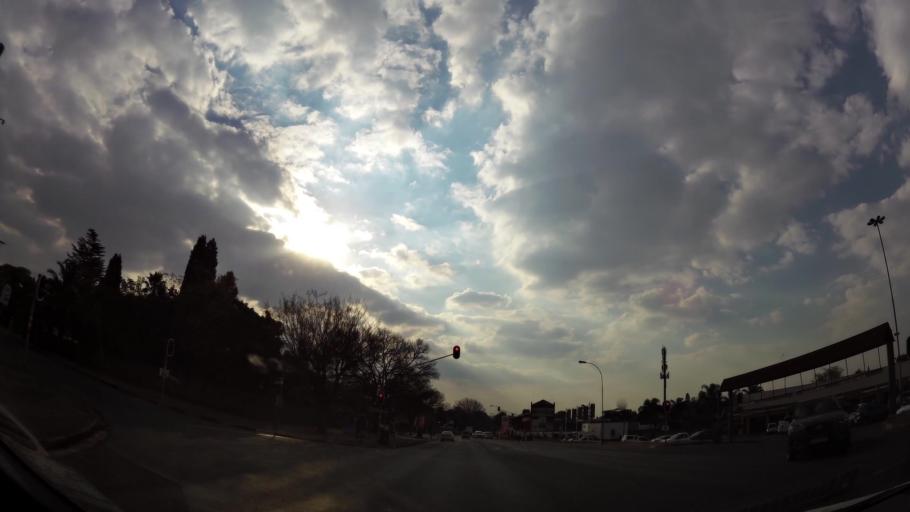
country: ZA
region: Gauteng
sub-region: Ekurhuleni Metropolitan Municipality
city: Germiston
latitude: -26.2391
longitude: 28.1758
